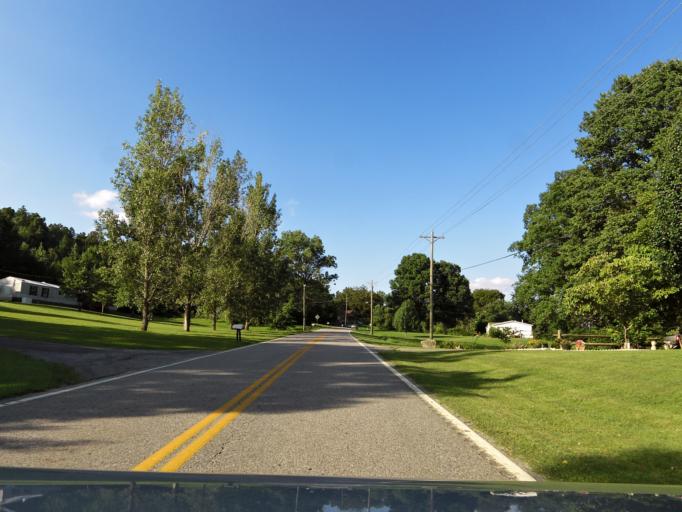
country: US
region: Tennessee
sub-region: Blount County
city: Maryville
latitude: 35.6353
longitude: -84.0068
